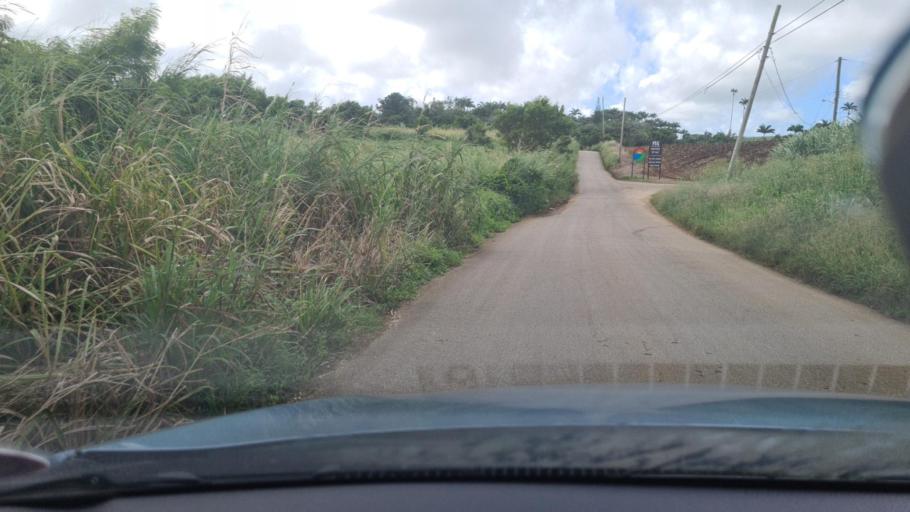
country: BB
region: Saint Joseph
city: Bathsheba
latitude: 13.1947
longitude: -59.5278
